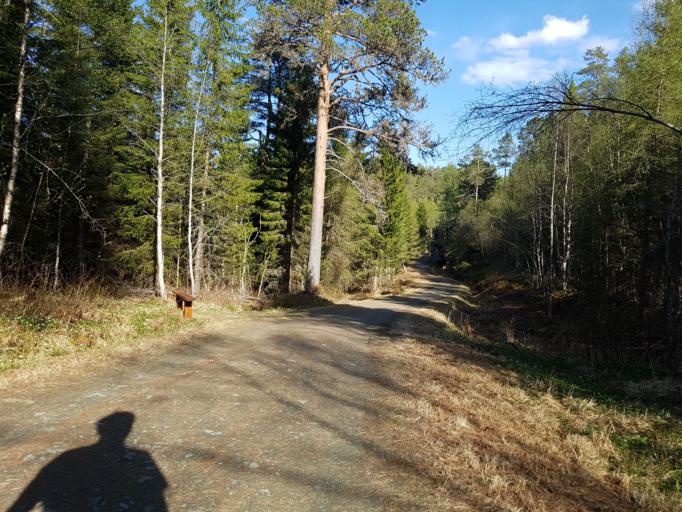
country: NO
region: Sor-Trondelag
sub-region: Trondheim
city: Trondheim
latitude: 63.4403
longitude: 10.3319
